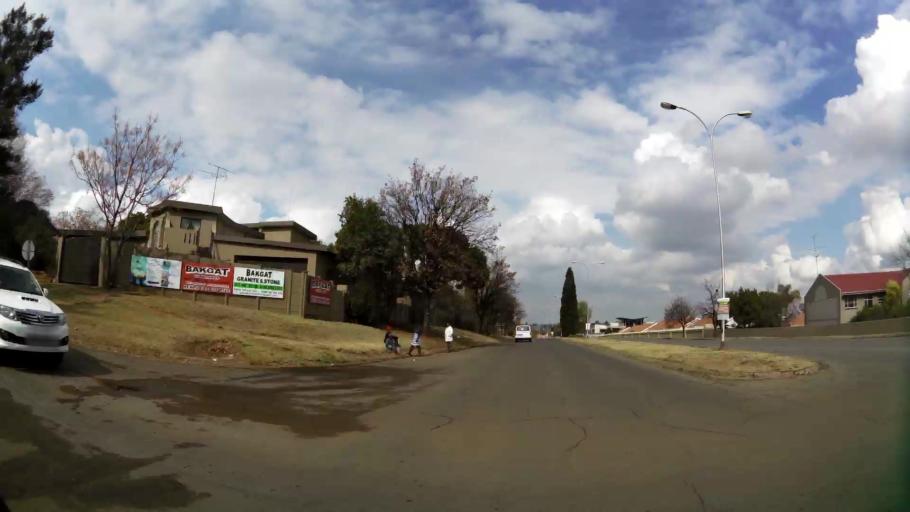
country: ZA
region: Gauteng
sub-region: Sedibeng District Municipality
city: Vanderbijlpark
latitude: -26.7386
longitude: 27.8440
